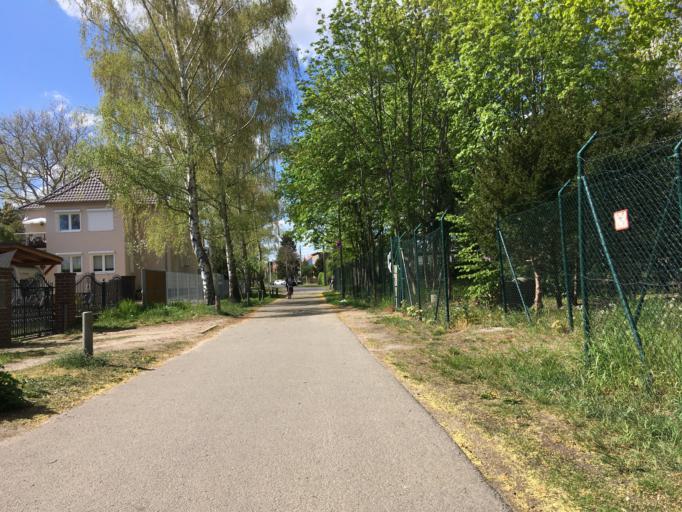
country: DE
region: Berlin
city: Mahlsdorf
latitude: 52.5174
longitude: 13.6217
